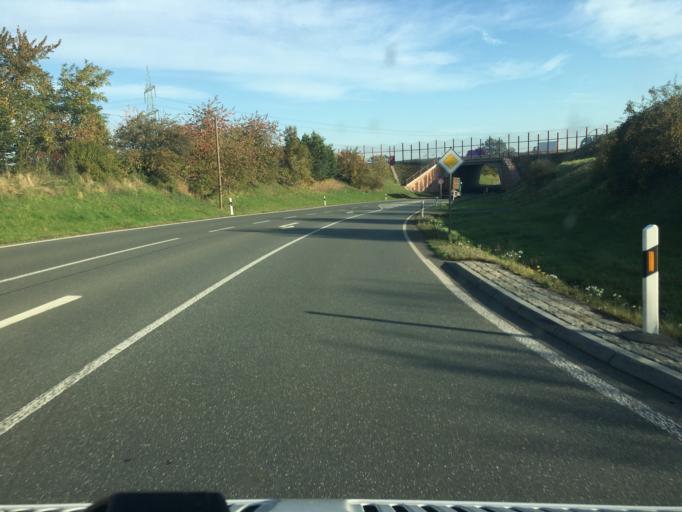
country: DE
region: Thuringia
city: Heyersdorf
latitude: 50.8489
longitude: 12.3345
